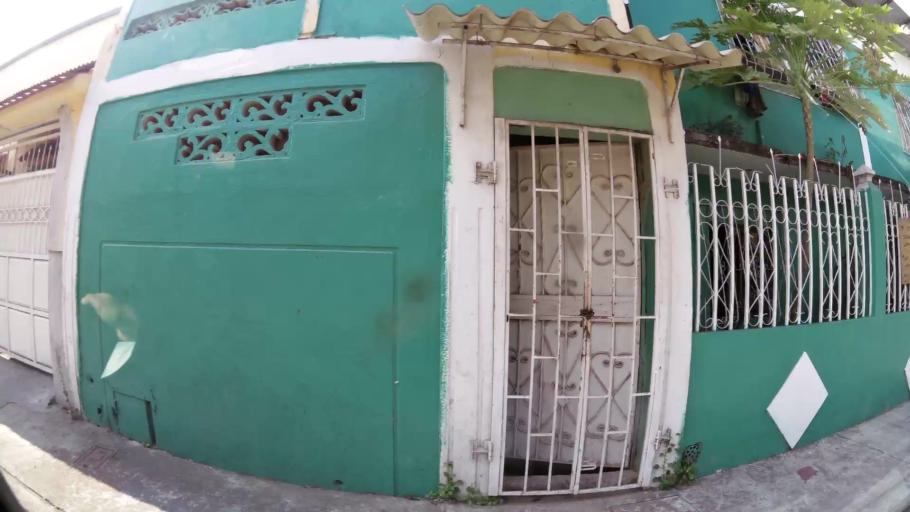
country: EC
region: Guayas
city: Guayaquil
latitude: -2.2616
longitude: -79.8865
